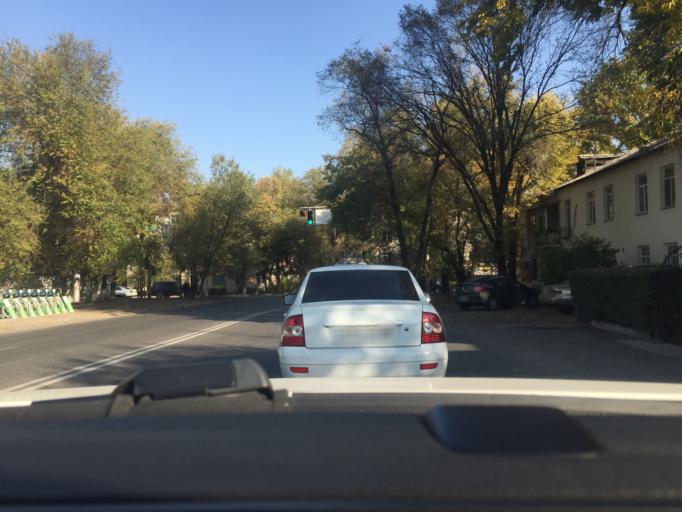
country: KZ
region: Almaty Qalasy
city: Almaty
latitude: 43.2448
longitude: 76.9080
